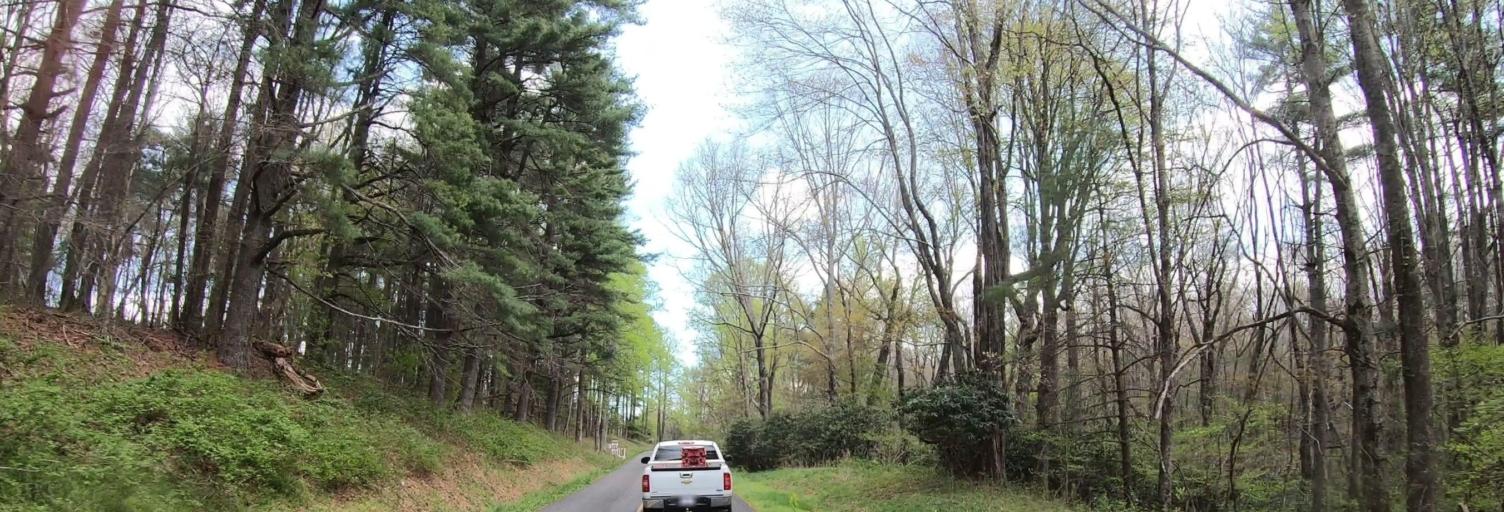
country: US
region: Virginia
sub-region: Carroll County
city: Cana
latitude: 36.6597
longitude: -80.7000
